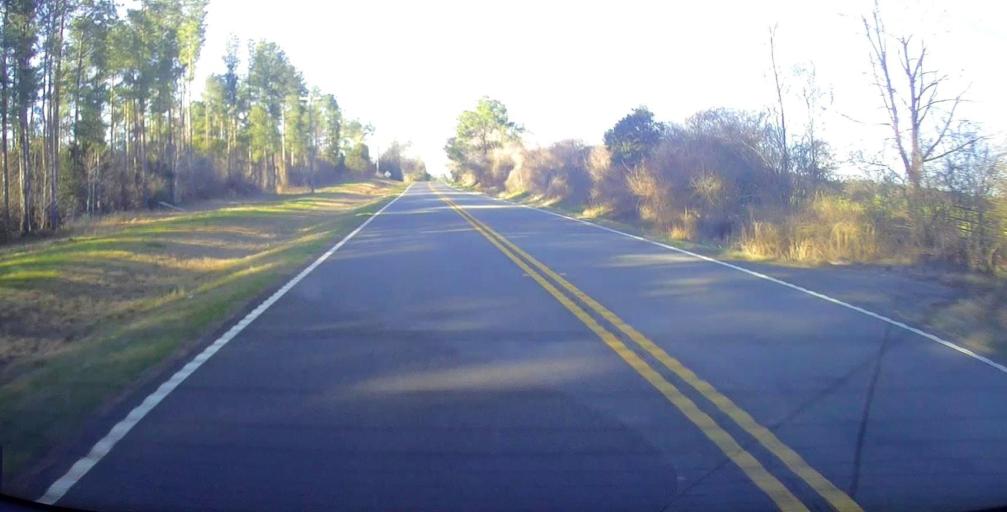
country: US
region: Georgia
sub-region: Sumter County
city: Americus
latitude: 32.0176
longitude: -84.2192
